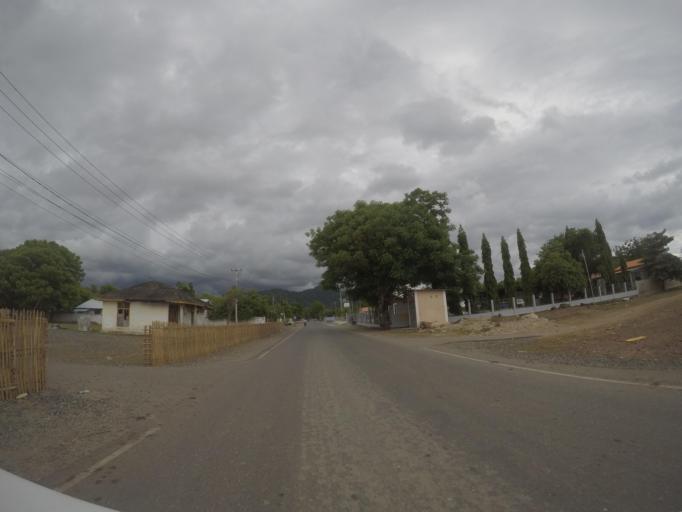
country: TL
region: Liquica
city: Maubara
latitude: -8.7841
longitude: 125.1014
